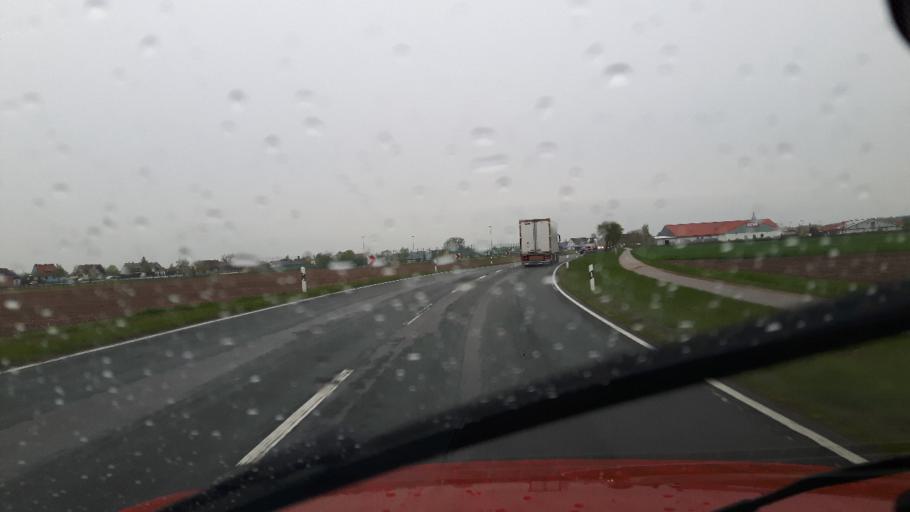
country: DE
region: Bavaria
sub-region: Regierungsbezirk Mittelfranken
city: Merkendorf
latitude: 49.1936
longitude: 10.7052
